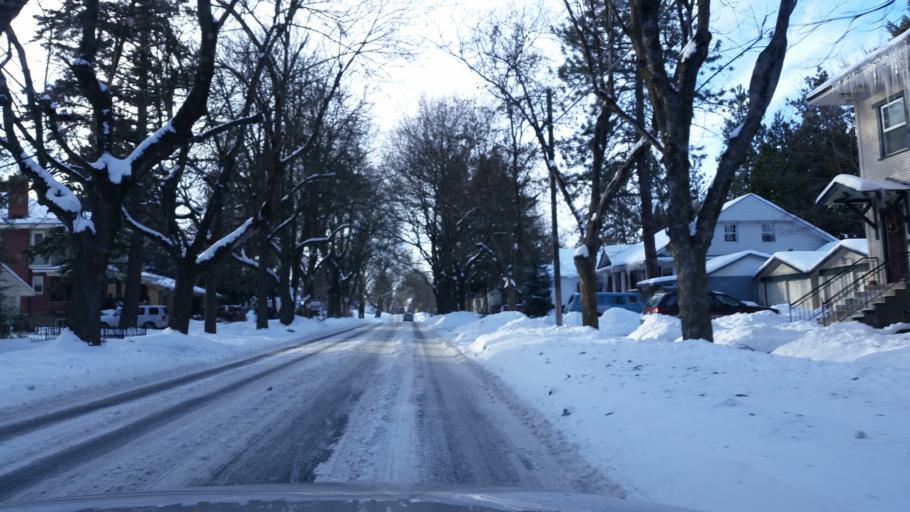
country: US
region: Washington
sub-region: Spokane County
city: Spokane
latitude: 47.6427
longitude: -117.4115
